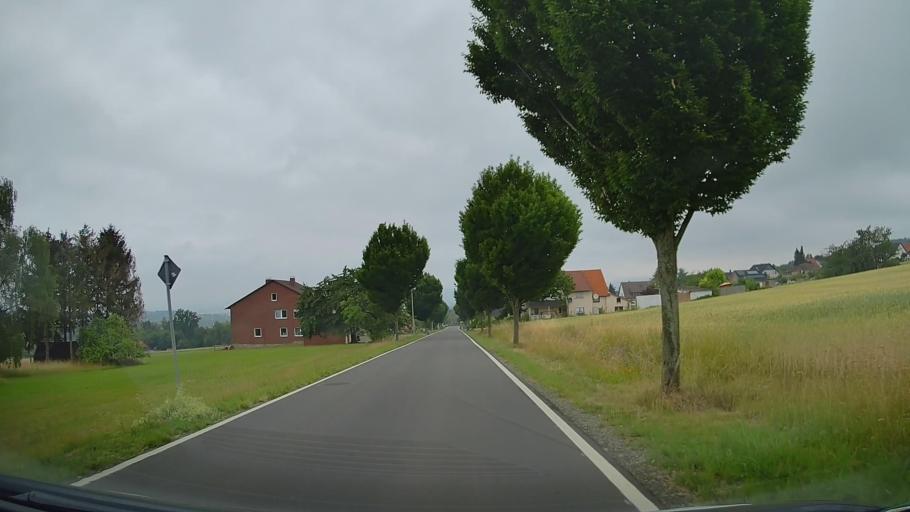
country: DE
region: Lower Saxony
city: Rinteln
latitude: 52.1349
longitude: 9.1008
